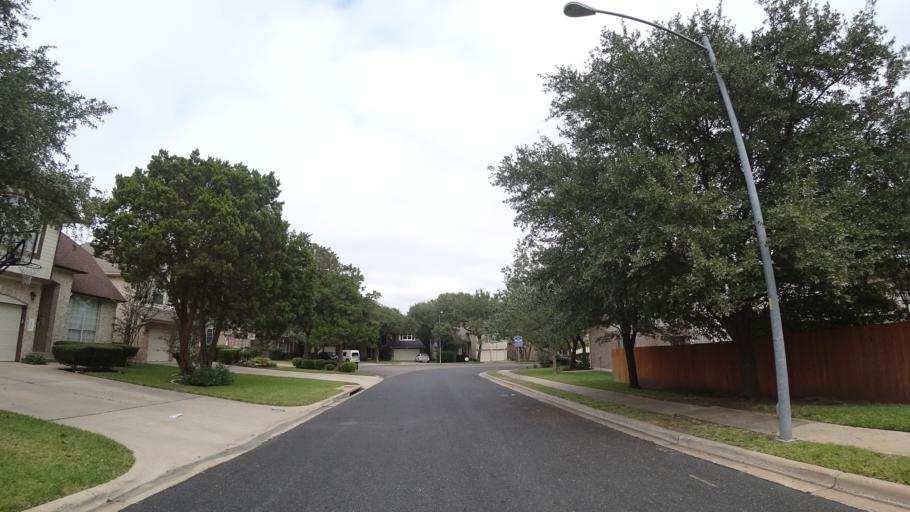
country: US
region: Texas
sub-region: Travis County
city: Shady Hollow
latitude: 30.2221
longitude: -97.8755
